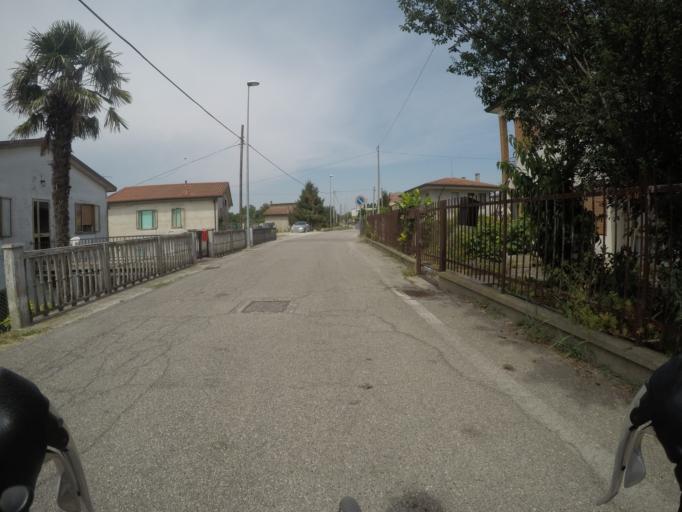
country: IT
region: Veneto
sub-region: Provincia di Rovigo
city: Villanova del Ghebbo Canton
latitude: 45.0505
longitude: 11.6489
